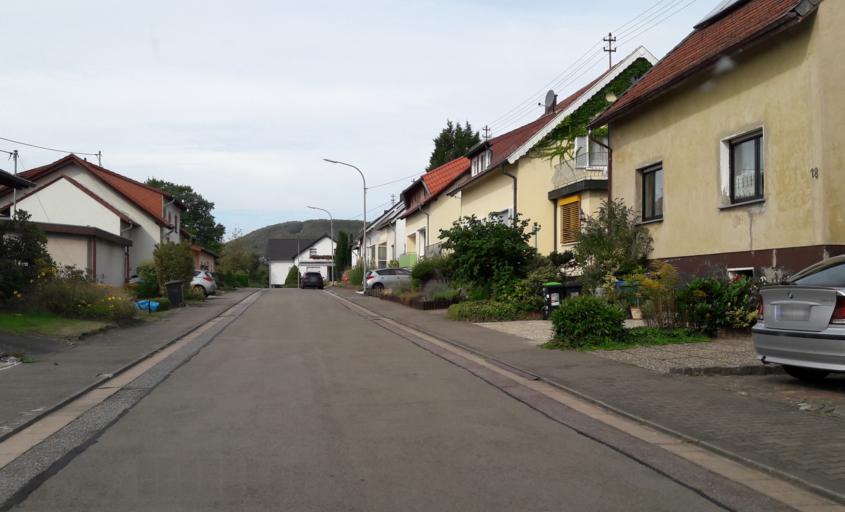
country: DE
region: Saarland
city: Oberthal
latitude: 49.5169
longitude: 7.0885
